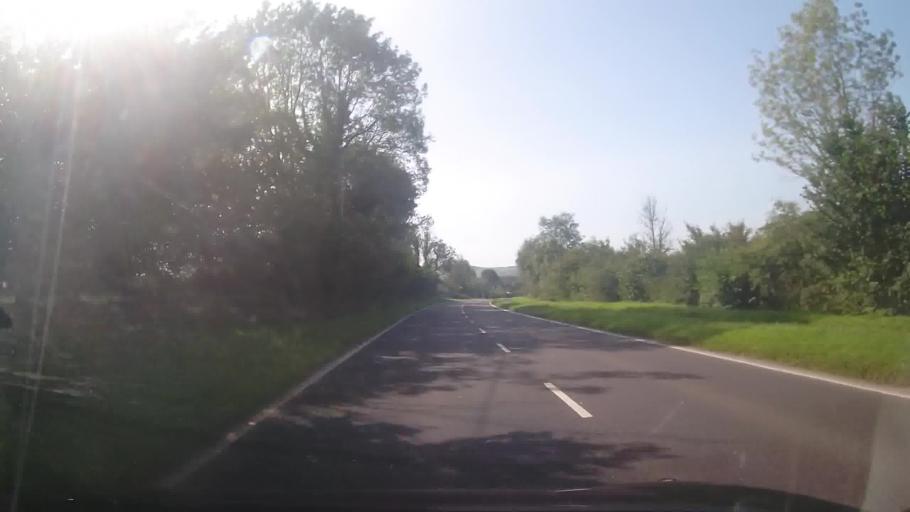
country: GB
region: Wales
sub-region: Carmarthenshire
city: Llandovery
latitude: 52.1112
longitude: -3.6331
